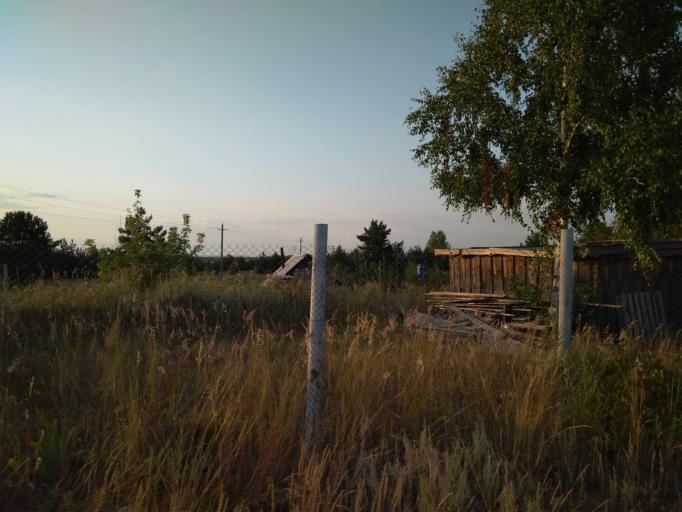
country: RU
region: Ulyanovsk
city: Staraya Mayna
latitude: 54.6444
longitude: 49.0481
